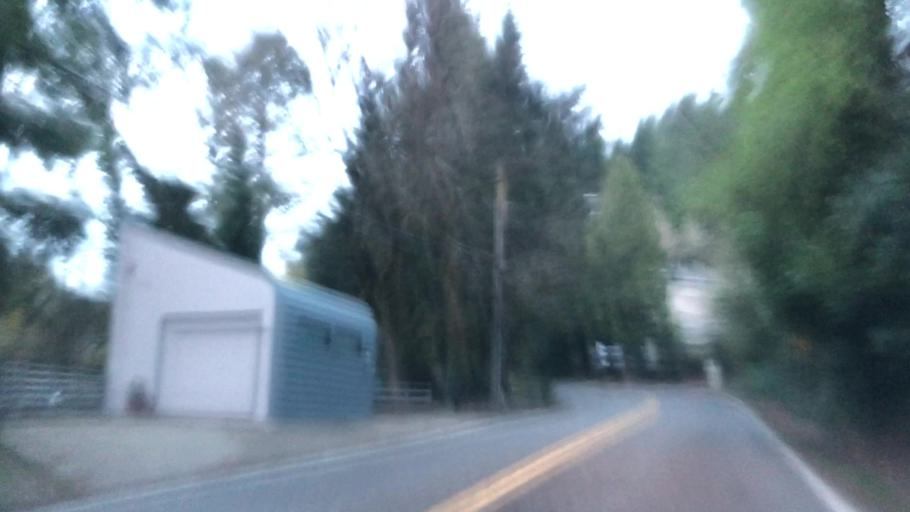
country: US
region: Oregon
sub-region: Multnomah County
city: Portland
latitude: 45.4956
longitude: -122.7120
